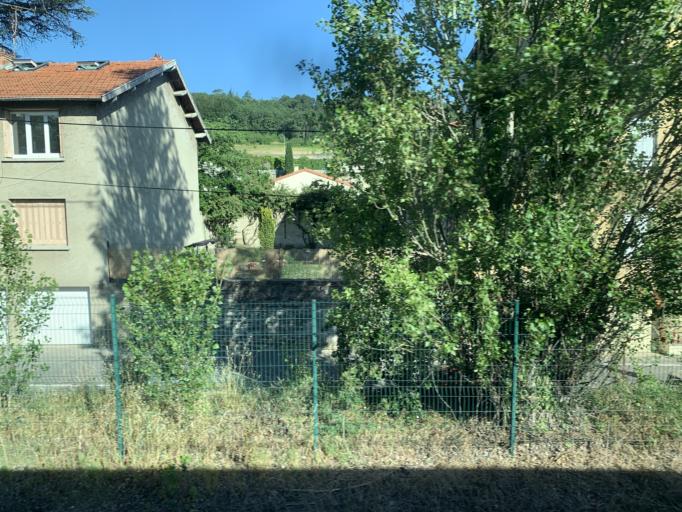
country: FR
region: Rhone-Alpes
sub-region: Departement du Rhone
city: Vernaison
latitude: 45.6451
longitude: 4.8131
